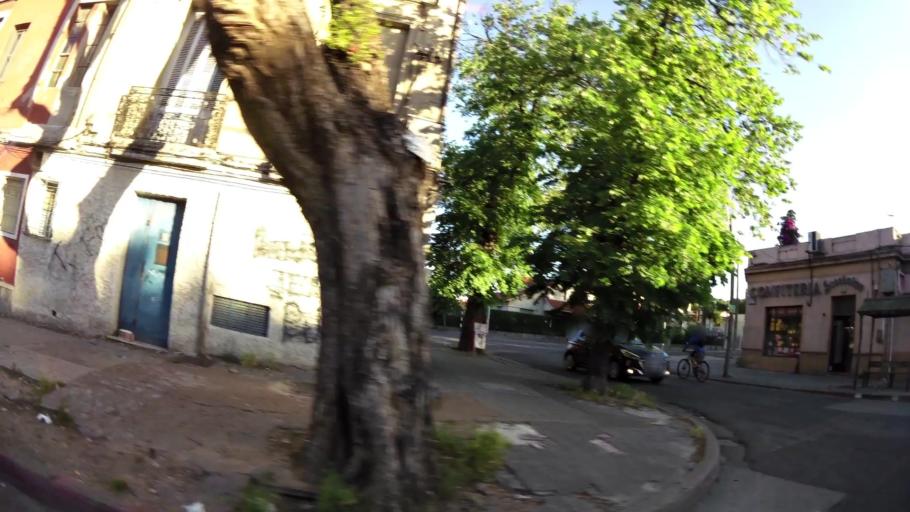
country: UY
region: Montevideo
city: Montevideo
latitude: -34.8515
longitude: -56.2063
